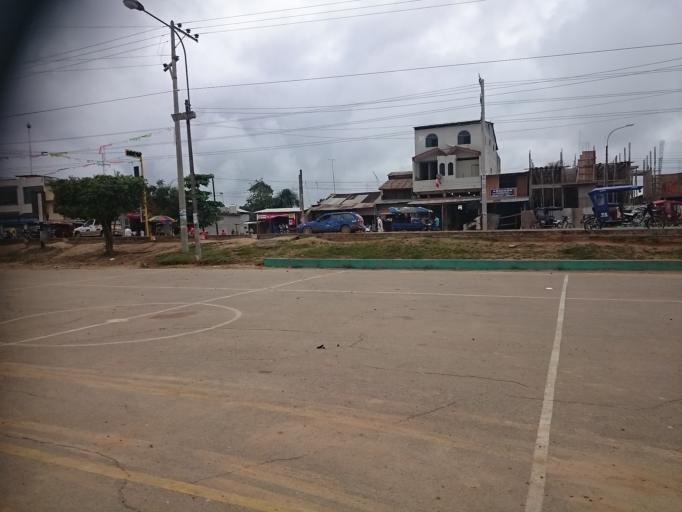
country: PE
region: Ucayali
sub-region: Provincia de Coronel Portillo
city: Campoverde
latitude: -8.4750
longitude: -74.8060
